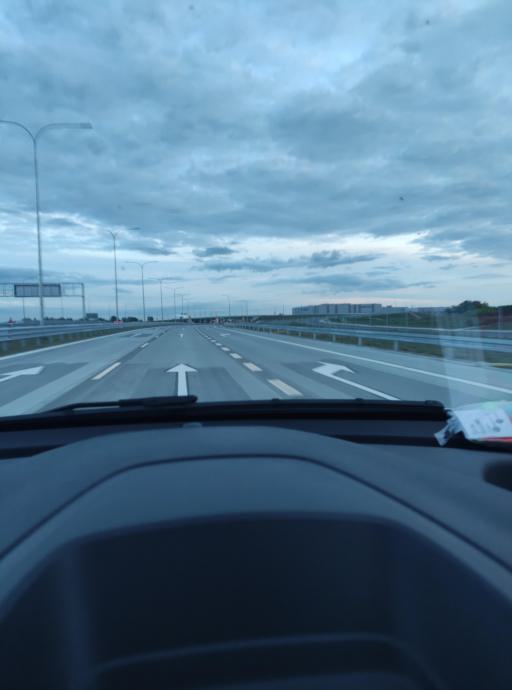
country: PL
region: Masovian Voivodeship
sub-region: Powiat piaseczynski
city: Mysiadlo
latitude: 52.1215
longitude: 20.9872
